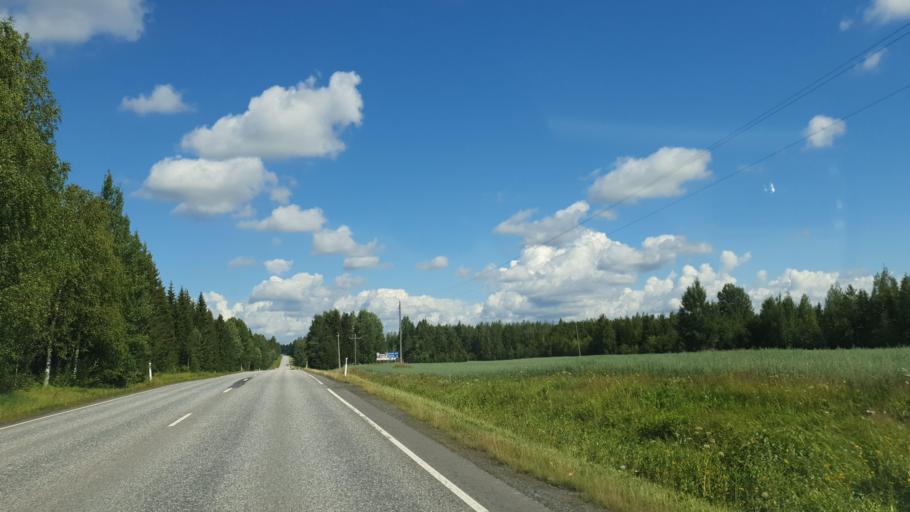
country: FI
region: Northern Savo
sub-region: Ylae-Savo
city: Sonkajaervi
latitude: 63.7303
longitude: 27.3755
